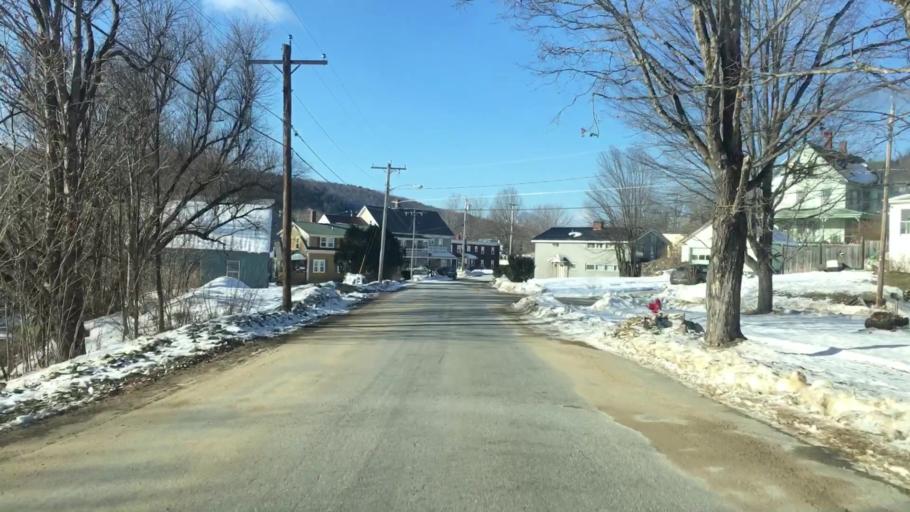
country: US
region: Maine
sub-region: Oxford County
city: West Paris
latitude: 44.3243
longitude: -70.5723
